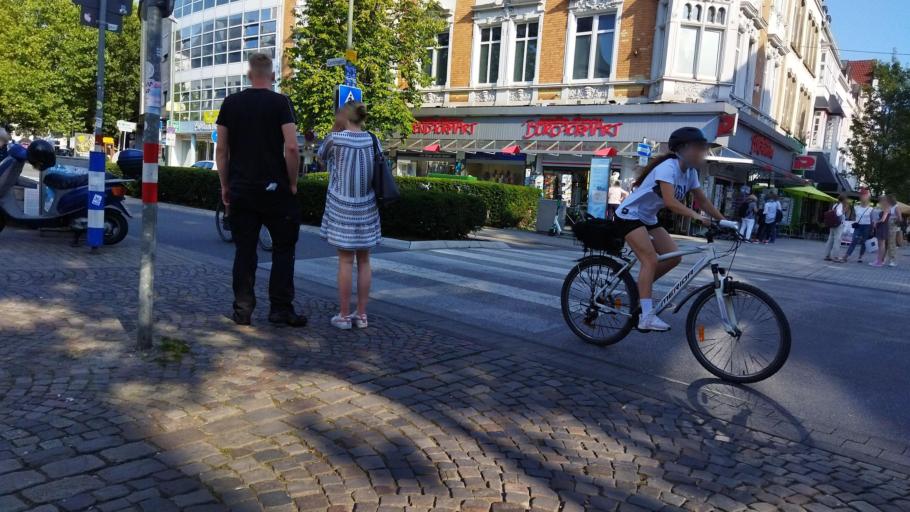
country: DE
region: Lower Saxony
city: Osnabrueck
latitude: 52.2764
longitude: 8.0424
